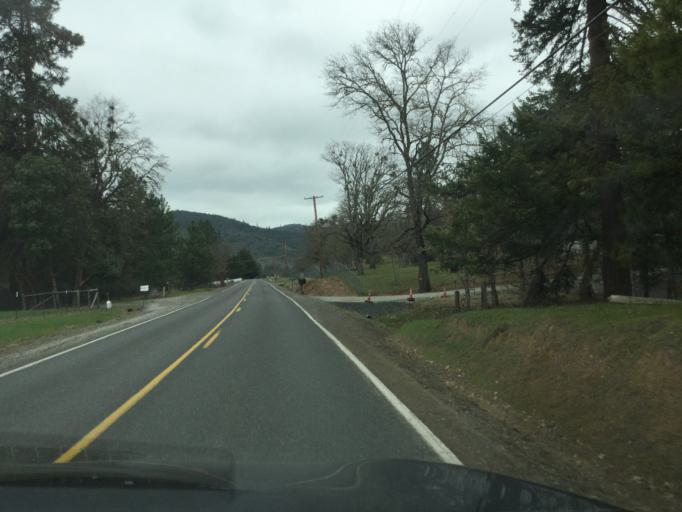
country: US
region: Oregon
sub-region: Jackson County
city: Gold Hill
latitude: 42.3980
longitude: -123.0137
